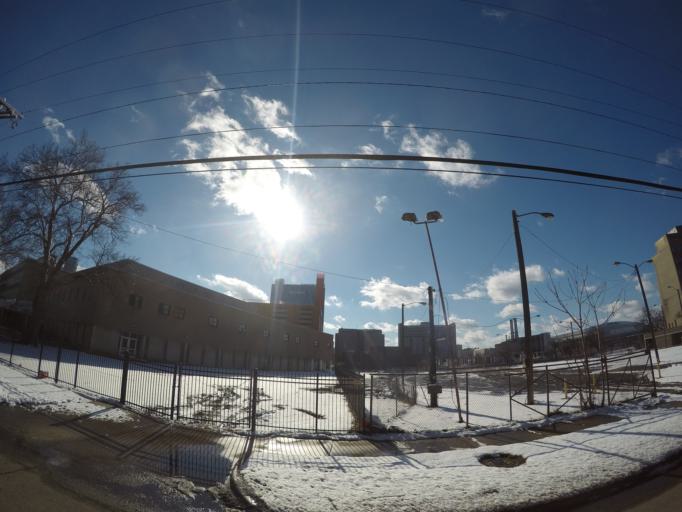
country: US
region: Michigan
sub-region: Wayne County
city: Detroit
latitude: 42.3380
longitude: -83.0373
